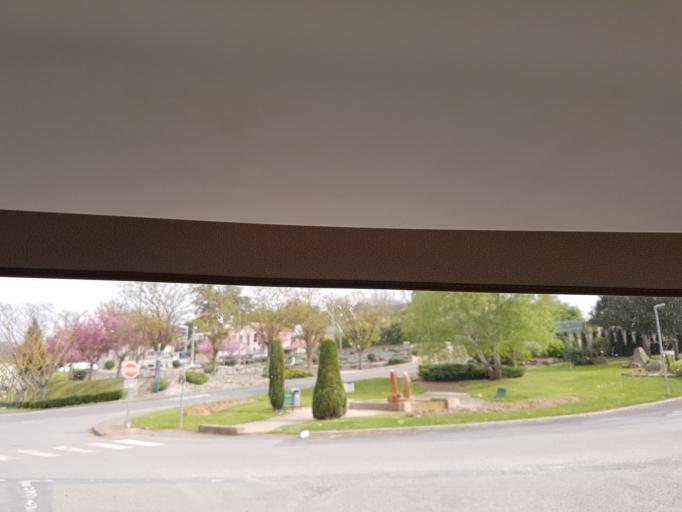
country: FR
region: Languedoc-Roussillon
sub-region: Departement de l'Aude
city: Esperaza
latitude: 42.9339
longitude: 2.2177
